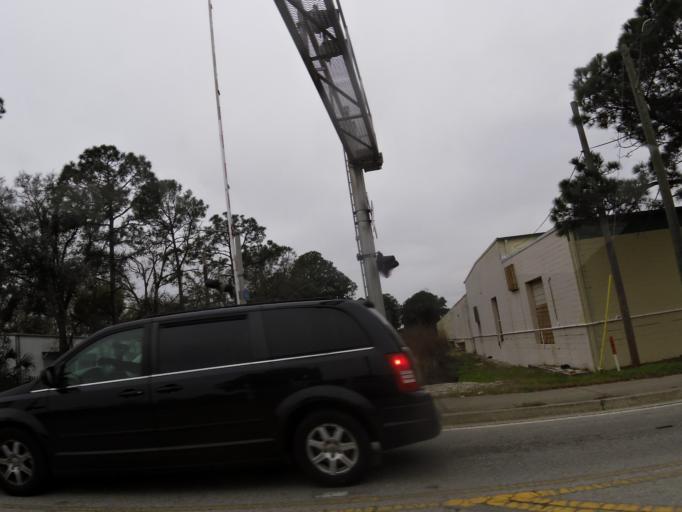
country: US
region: Florida
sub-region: Duval County
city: Jacksonville
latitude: 30.3557
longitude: -81.6971
